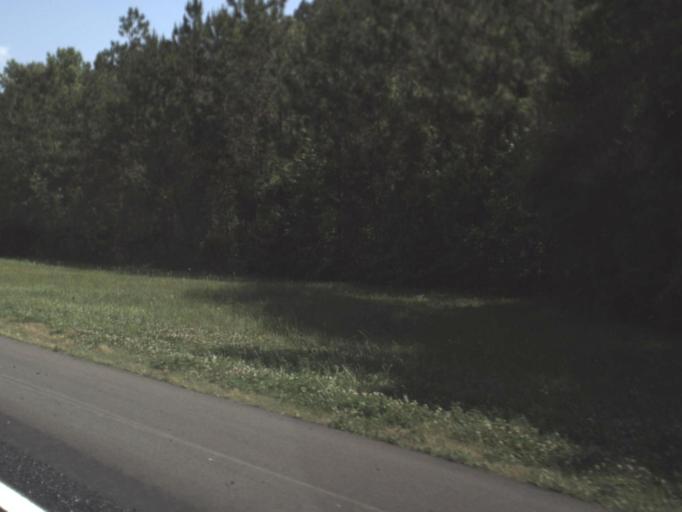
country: US
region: Florida
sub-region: Nassau County
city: Yulee
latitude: 30.6425
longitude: -81.6579
